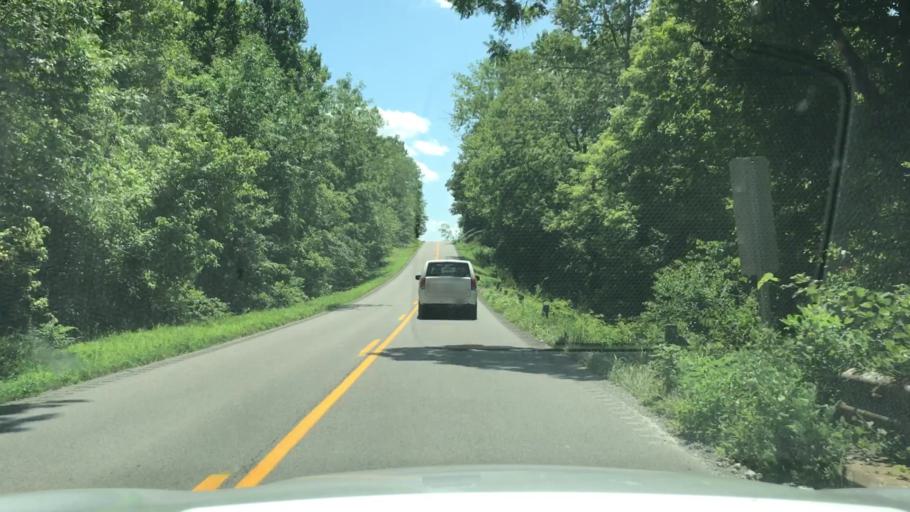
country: US
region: Kentucky
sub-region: Christian County
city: Hopkinsville
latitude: 36.9071
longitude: -87.4453
